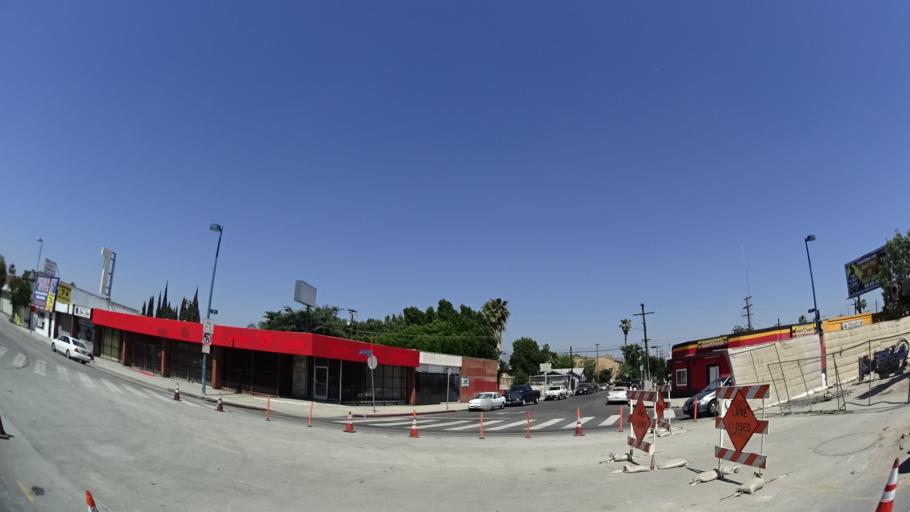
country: US
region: California
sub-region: Los Angeles County
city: North Hollywood
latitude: 34.1739
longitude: -118.3802
